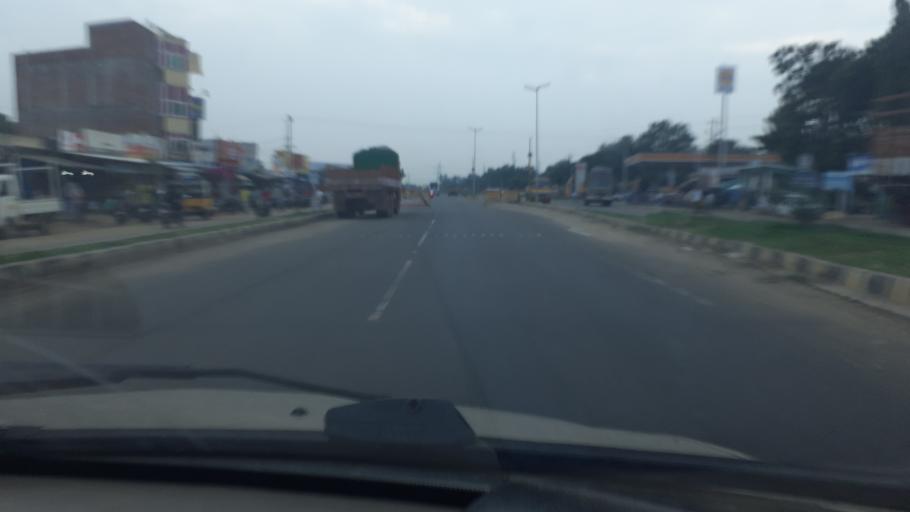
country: IN
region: Tamil Nadu
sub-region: Thoothukkudi
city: Korampallam
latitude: 8.7776
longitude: 78.0919
